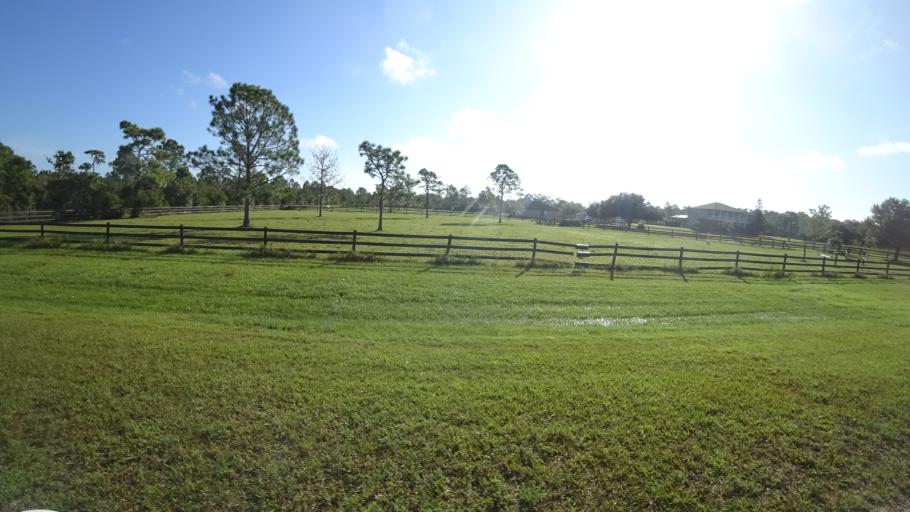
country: US
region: Florida
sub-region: Sarasota County
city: The Meadows
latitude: 27.4238
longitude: -82.3437
